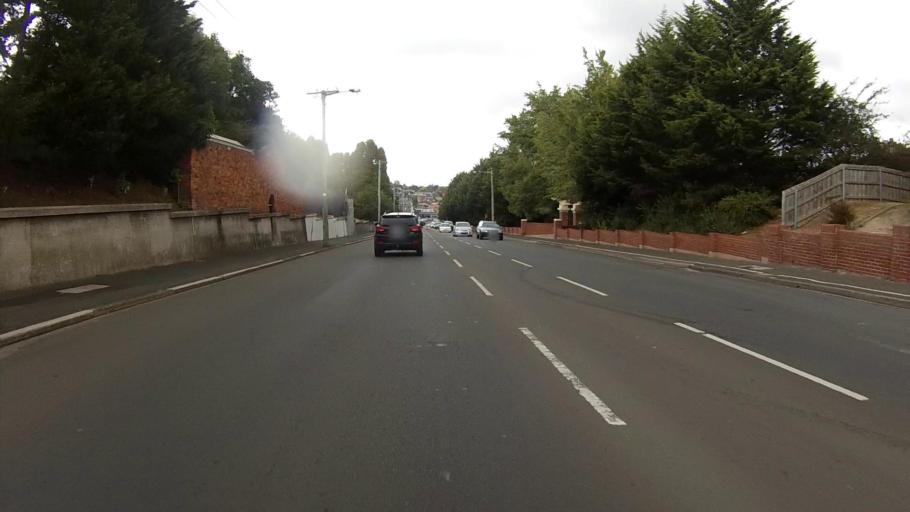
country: AU
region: Tasmania
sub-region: Glenorchy
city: Moonah
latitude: -42.8535
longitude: 147.3009
